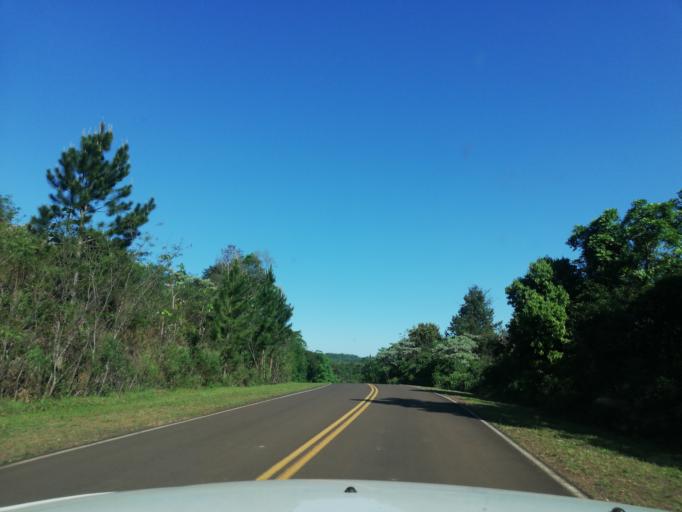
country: AR
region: Misiones
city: Arroyo del Medio
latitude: -27.6589
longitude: -55.4008
